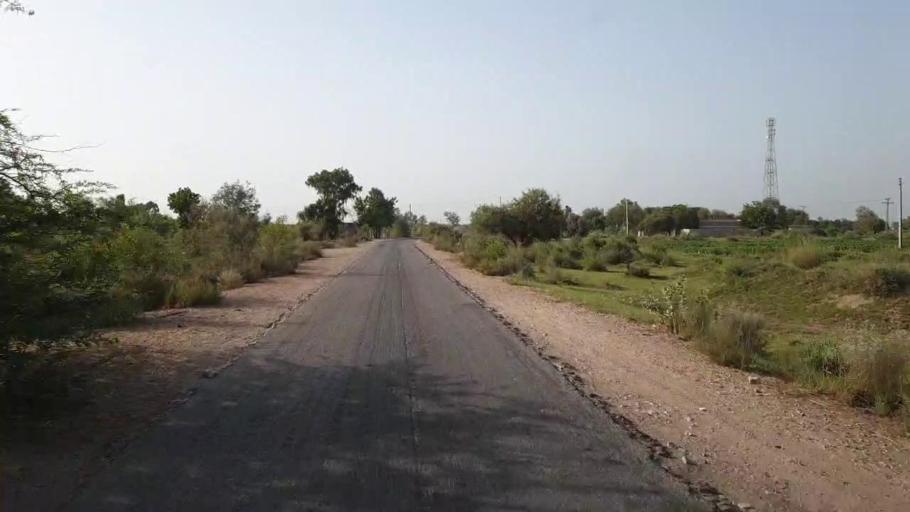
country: PK
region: Sindh
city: Jam Sahib
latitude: 26.4800
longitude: 68.8600
